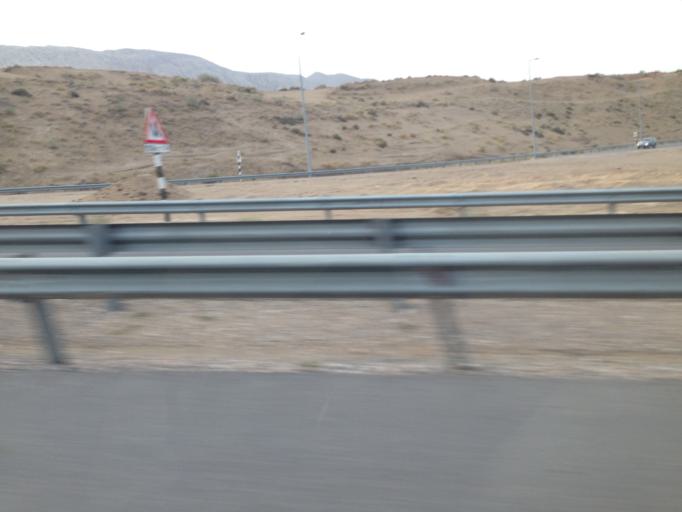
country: OM
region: Muhafazat Masqat
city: Bawshar
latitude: 23.5695
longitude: 58.4093
